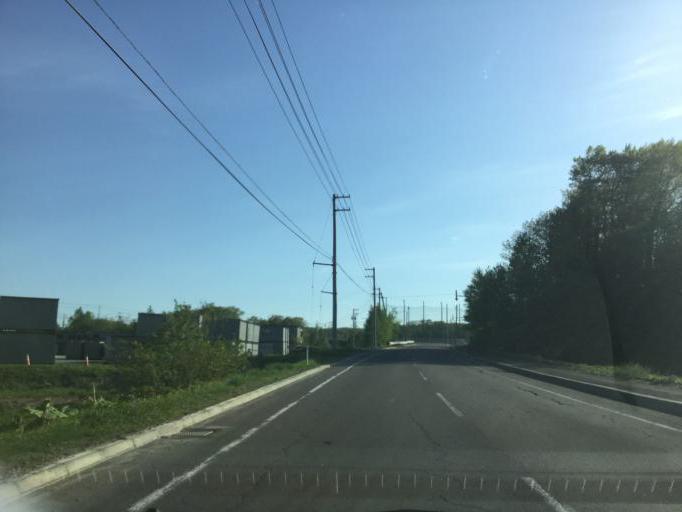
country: JP
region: Hokkaido
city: Kitahiroshima
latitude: 43.0021
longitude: 141.5476
